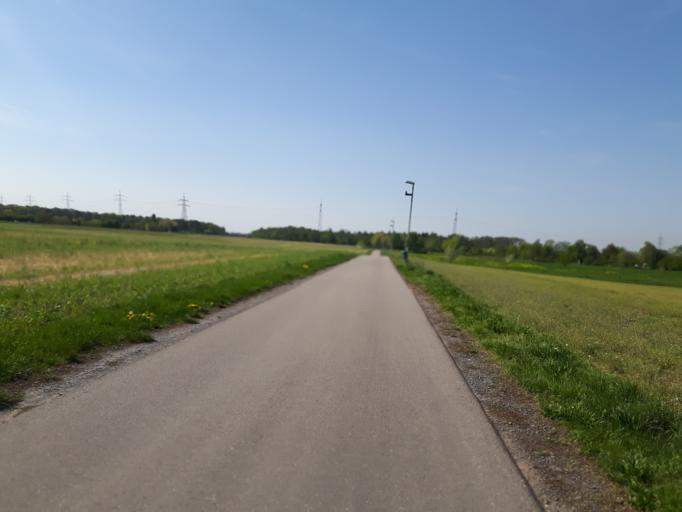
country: DE
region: Baden-Wuerttemberg
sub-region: Karlsruhe Region
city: Sankt Leon-Rot
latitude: 49.2780
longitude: 8.5904
